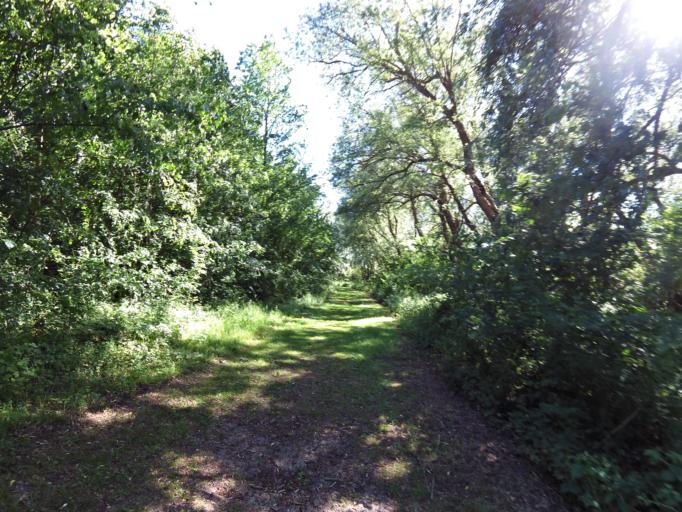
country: NL
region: South Holland
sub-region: Gemeente Goeree-Overflakkee
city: Goedereede
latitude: 51.8170
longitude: 4.0336
